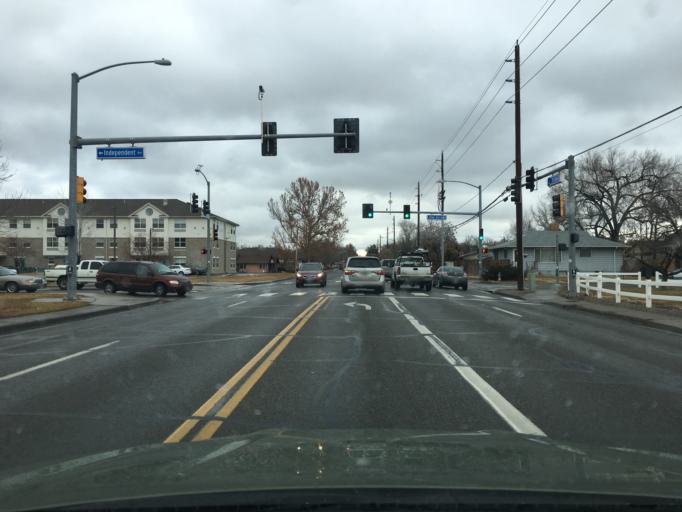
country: US
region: Colorado
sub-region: Mesa County
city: Grand Junction
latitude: 39.0806
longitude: -108.5709
